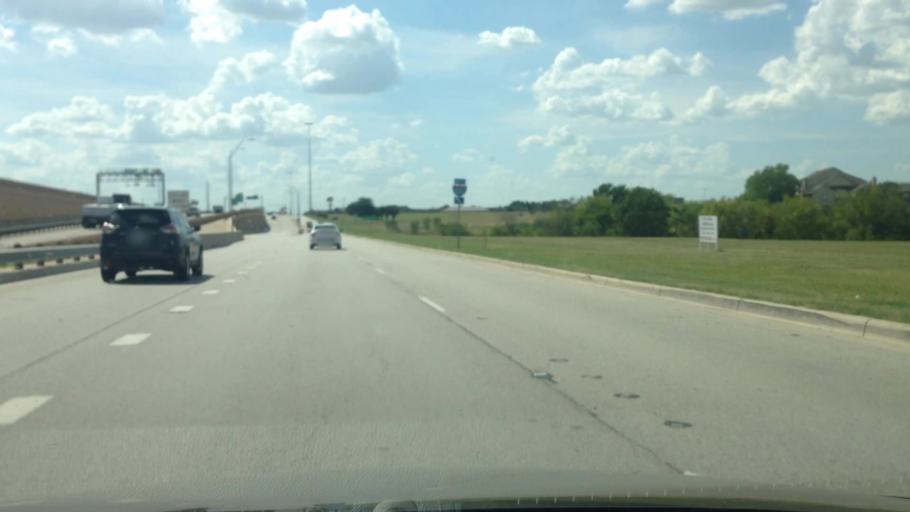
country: US
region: Texas
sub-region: Tarrant County
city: Watauga
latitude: 32.8401
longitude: -97.2816
